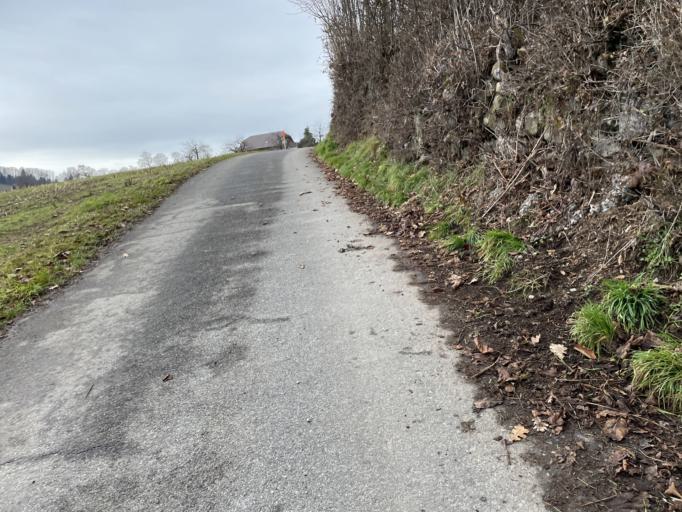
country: CH
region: Bern
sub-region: Bern-Mittelland District
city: Munsingen
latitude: 46.8674
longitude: 7.5344
